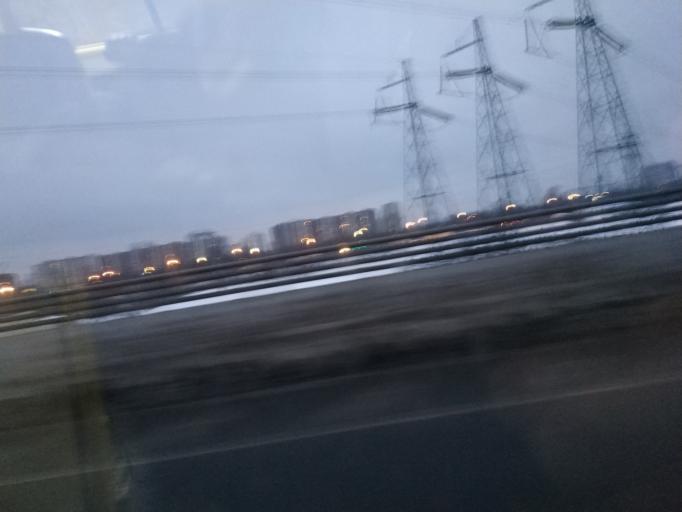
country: RU
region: Moscow
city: Zhulebino
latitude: 55.7091
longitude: 37.8501
